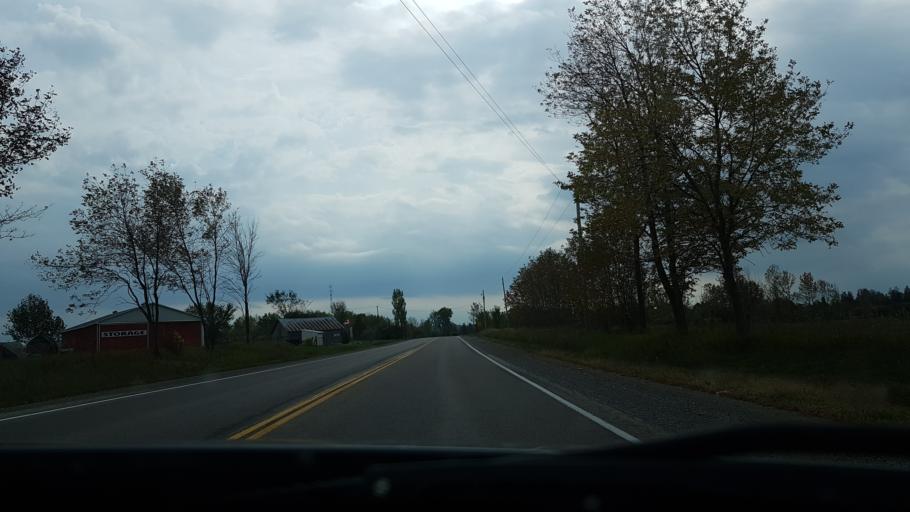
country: CA
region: Ontario
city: Omemee
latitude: 44.4639
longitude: -78.7625
